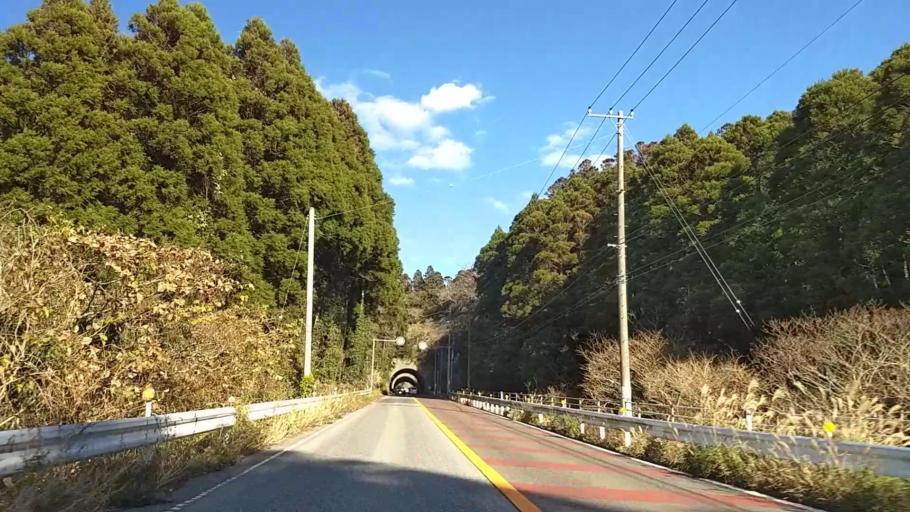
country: JP
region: Chiba
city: Ohara
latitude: 35.1955
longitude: 140.3656
